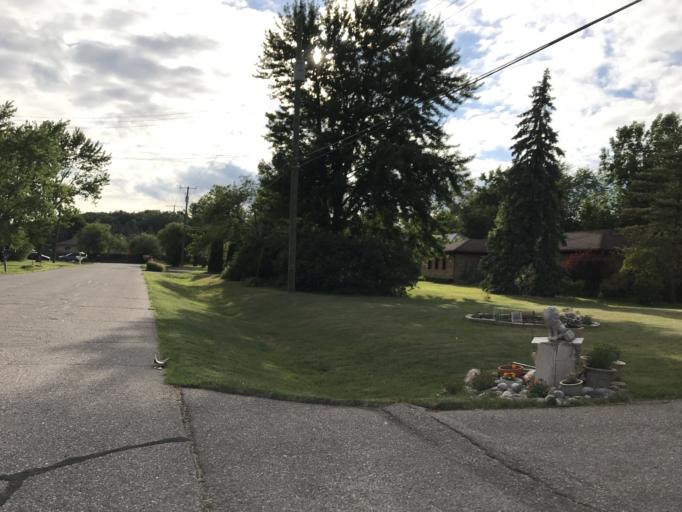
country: US
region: Michigan
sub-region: Oakland County
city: Farmington Hills
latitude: 42.4773
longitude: -83.3417
